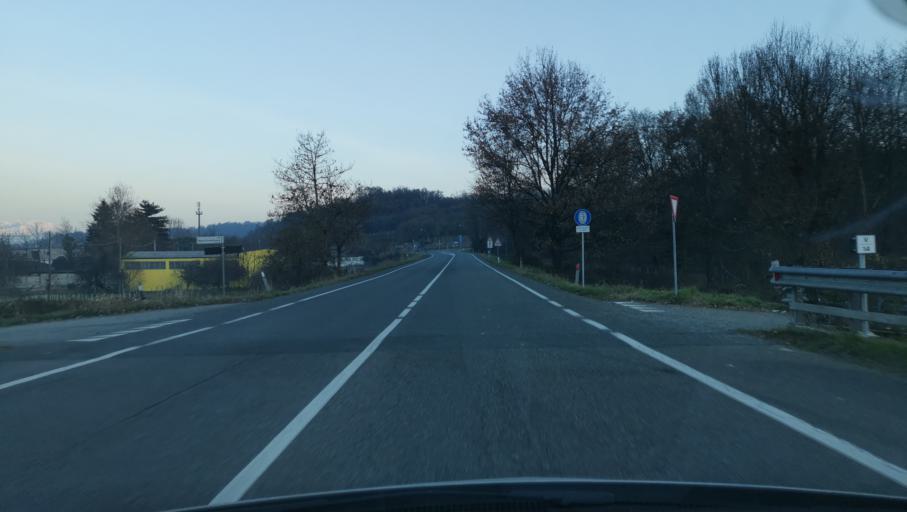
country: IT
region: Piedmont
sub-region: Provincia di Torino
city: Caluso
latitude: 45.3129
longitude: 7.8797
